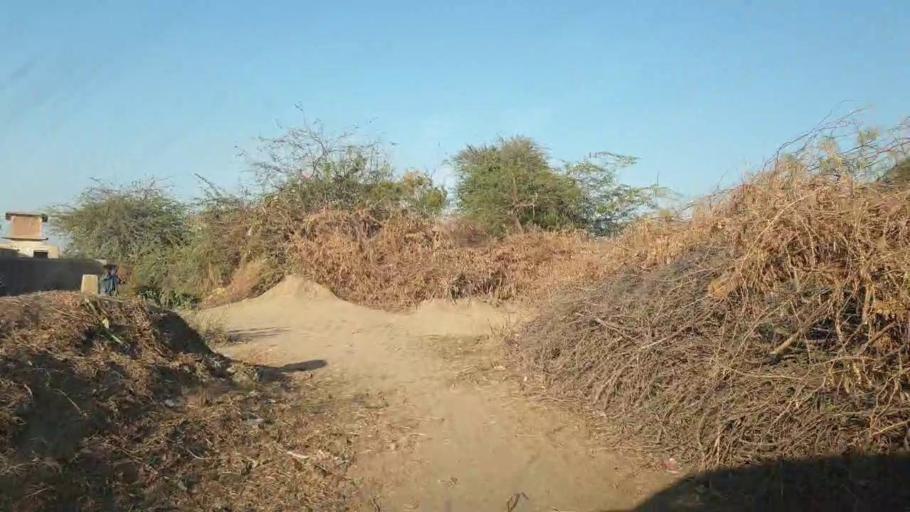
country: PK
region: Sindh
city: Chambar
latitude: 25.2846
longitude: 68.8012
